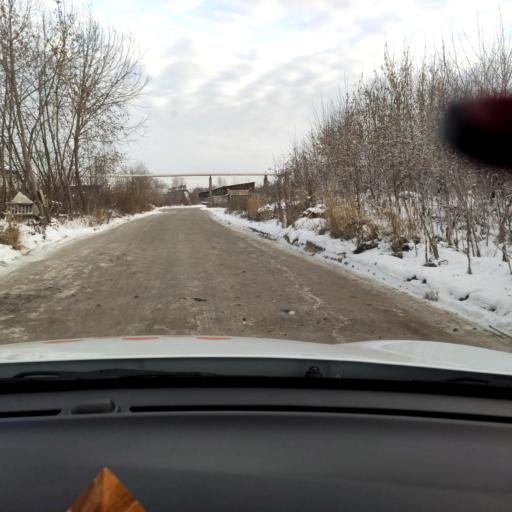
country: RU
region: Tatarstan
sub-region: Gorod Kazan'
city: Kazan
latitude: 55.7394
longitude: 49.1209
